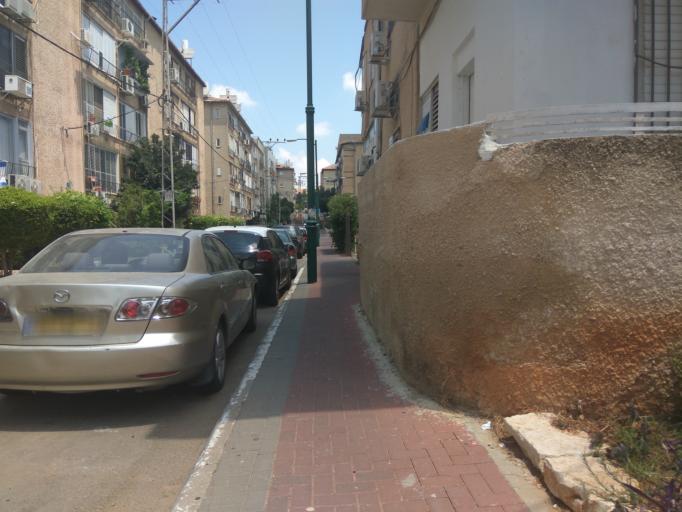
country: IL
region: Central District
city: Rishon LeZiyyon
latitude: 31.9622
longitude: 34.8057
